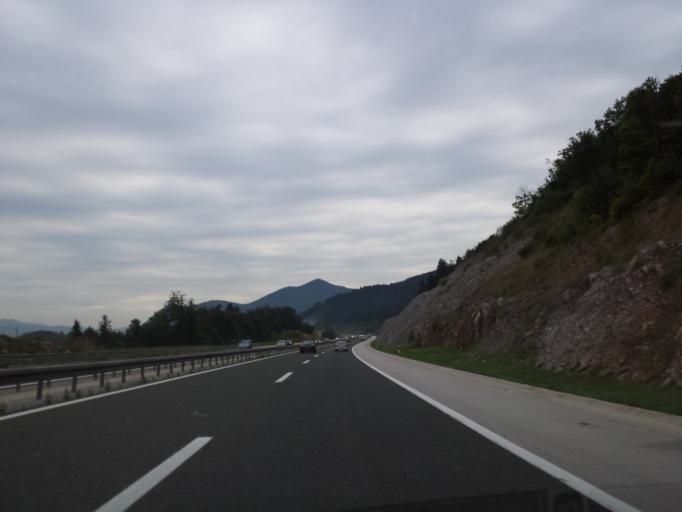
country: HR
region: Licko-Senjska
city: Otocac
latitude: 44.8424
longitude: 15.2432
